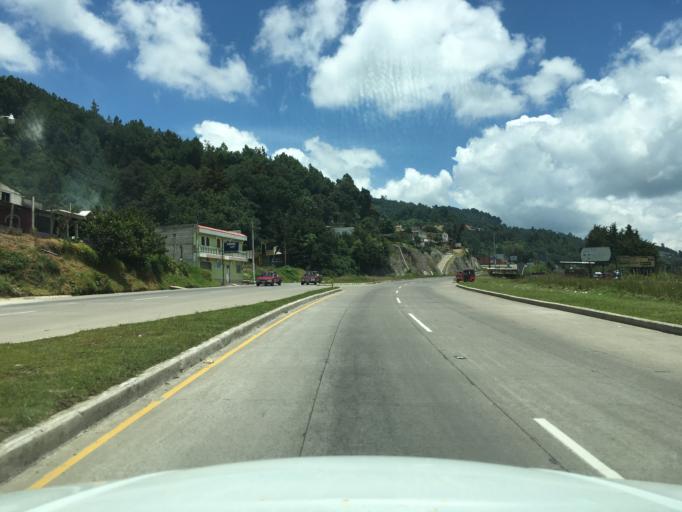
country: GT
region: Chimaltenango
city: Tecpan Guatemala
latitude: 14.7800
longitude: -90.9869
